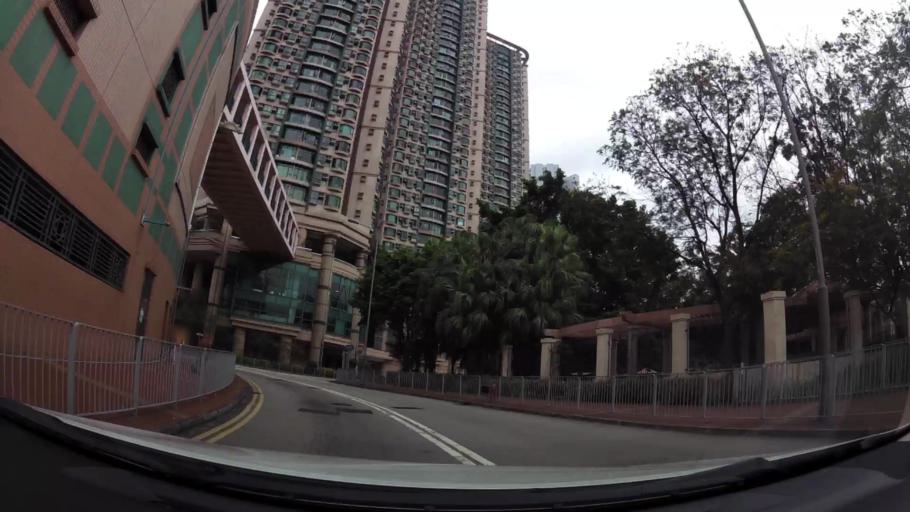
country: HK
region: Tuen Mun
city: Tuen Mun
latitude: 22.4010
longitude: 113.9746
